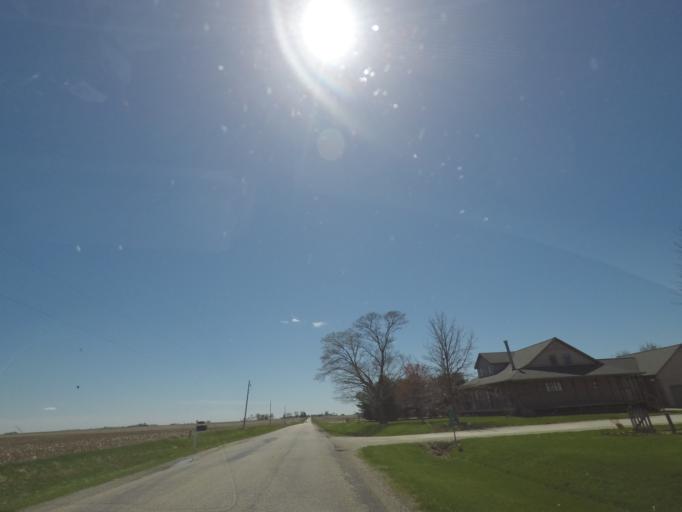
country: US
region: Illinois
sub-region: Logan County
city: Atlanta
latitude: 40.1809
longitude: -89.1939
